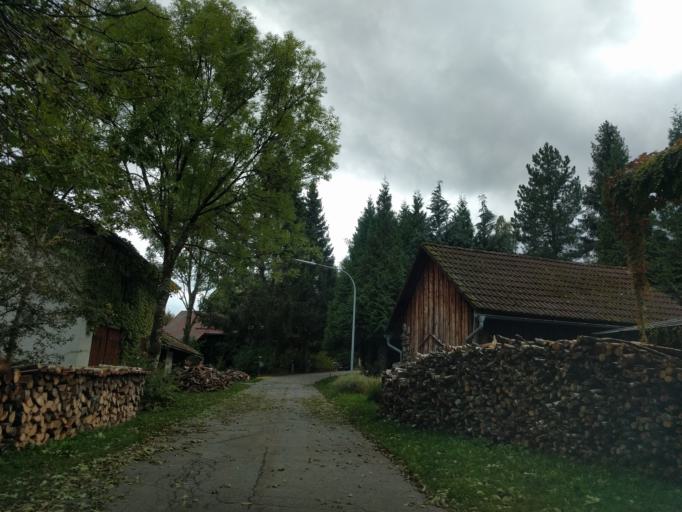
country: DE
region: Bavaria
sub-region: Lower Bavaria
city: Grafling
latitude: 48.8789
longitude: 12.9966
